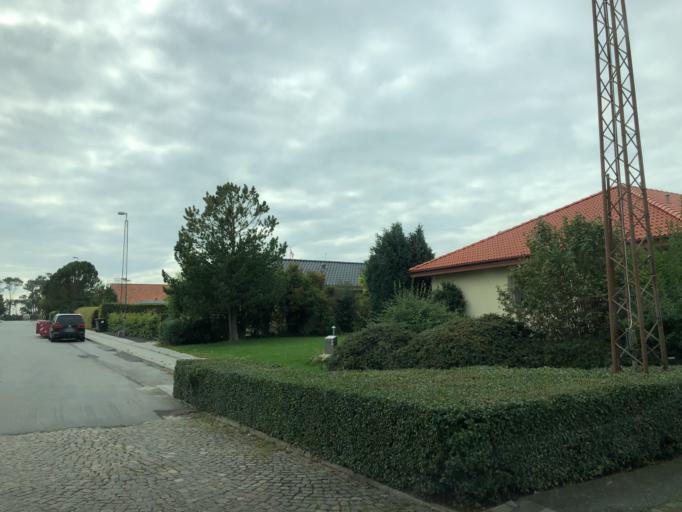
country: DK
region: South Denmark
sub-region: Sonderborg Kommune
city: Sonderborg
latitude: 54.8974
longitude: 9.8090
